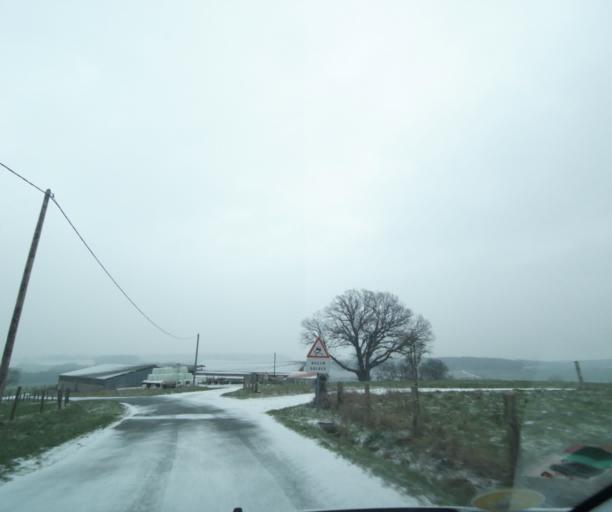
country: FR
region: Champagne-Ardenne
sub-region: Departement de la Haute-Marne
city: Wassy
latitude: 48.4758
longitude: 5.0372
